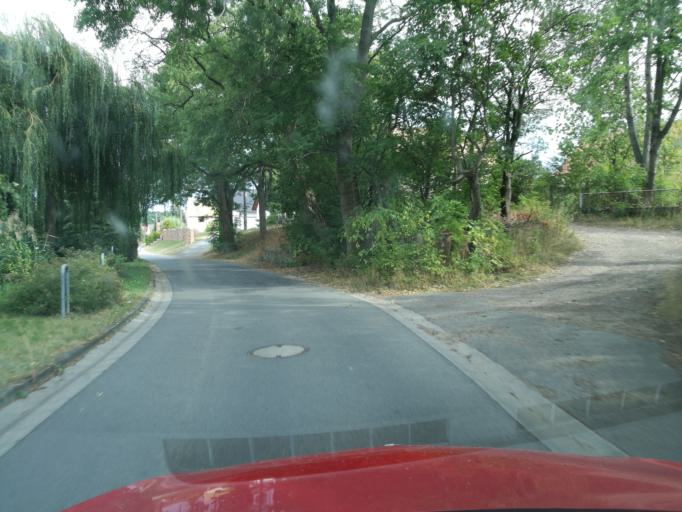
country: DE
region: Saxony
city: Oschatz
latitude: 51.2819
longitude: 13.0768
